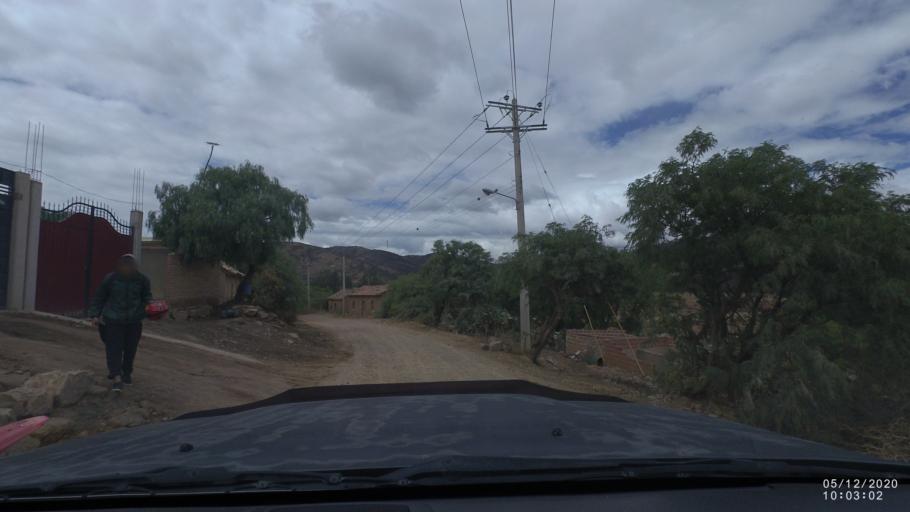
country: BO
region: Cochabamba
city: Sipe Sipe
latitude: -17.4546
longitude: -66.2864
